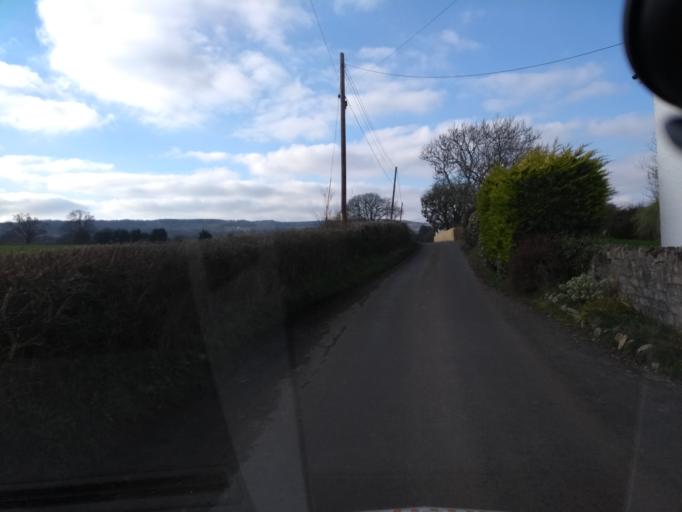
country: GB
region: England
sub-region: Somerset
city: Creech Saint Michael
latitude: 50.9517
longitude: -3.0382
